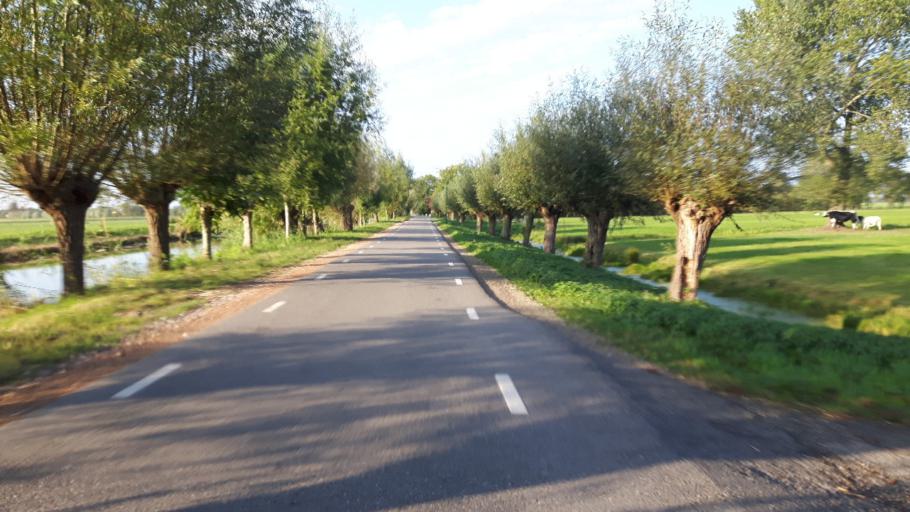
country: NL
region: Utrecht
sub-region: Gemeente Montfoort
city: Montfoort
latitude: 52.0606
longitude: 4.9405
